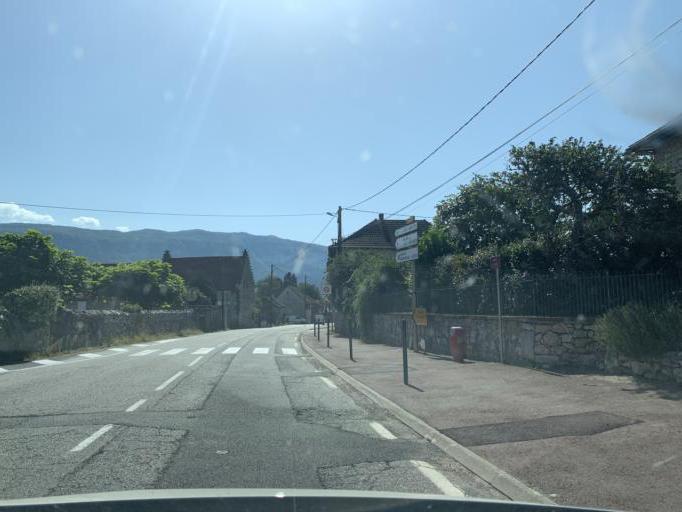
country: FR
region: Rhone-Alpes
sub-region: Departement de la Savoie
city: Yenne
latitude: 45.6761
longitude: 5.6776
